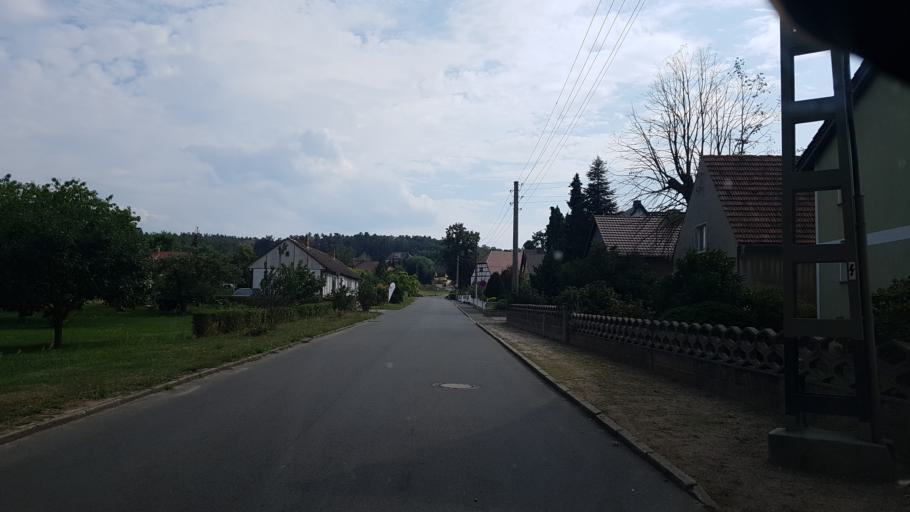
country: DE
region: Brandenburg
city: Grosskmehlen
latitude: 51.3764
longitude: 13.7238
